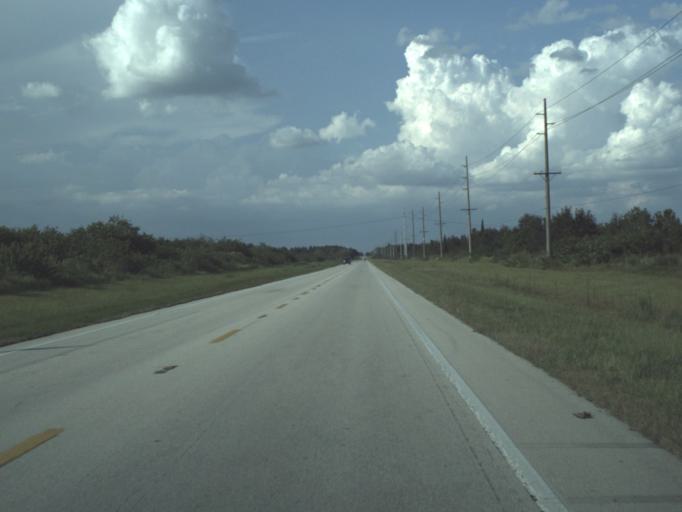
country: US
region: Florida
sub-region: Polk County
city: Mulberry
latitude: 27.8011
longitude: -81.9818
